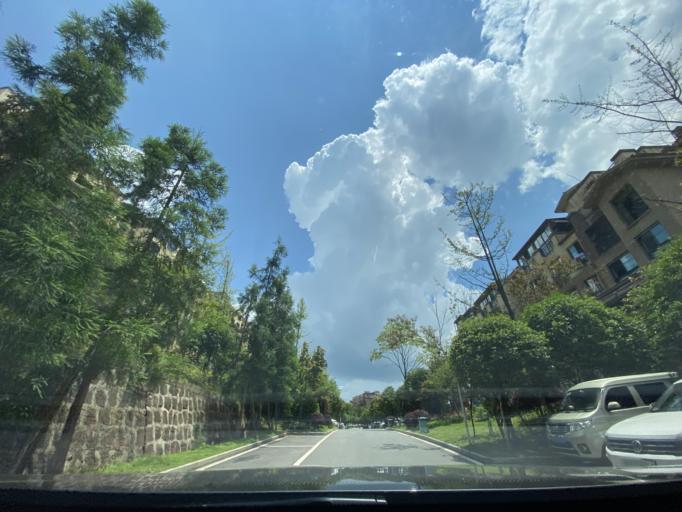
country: CN
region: Guizhou Sheng
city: Changqi
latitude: 28.5363
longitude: 105.9760
